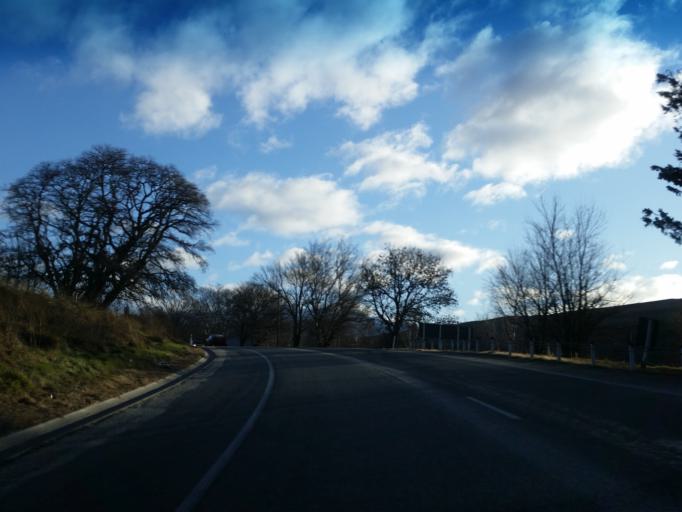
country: NZ
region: Otago
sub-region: Queenstown-Lakes District
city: Arrowtown
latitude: -44.9940
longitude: 168.7975
